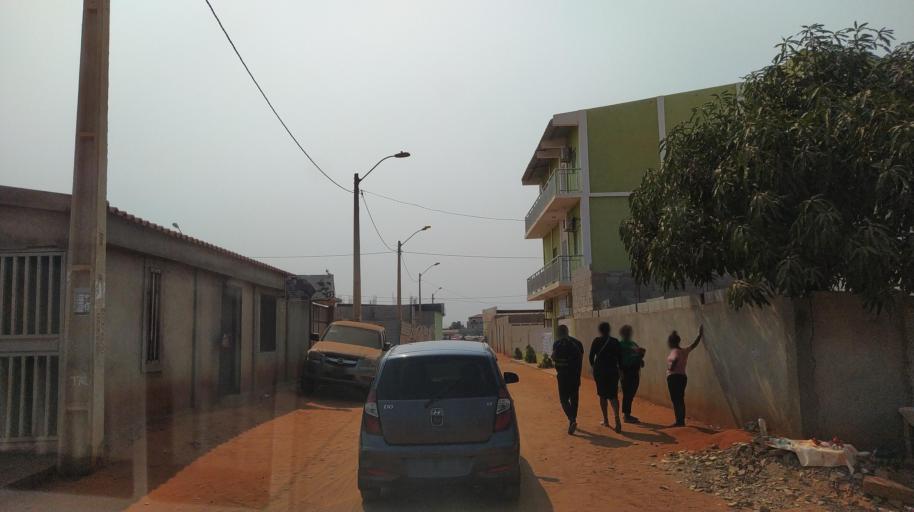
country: AO
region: Luanda
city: Luanda
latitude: -9.0638
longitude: 13.4170
